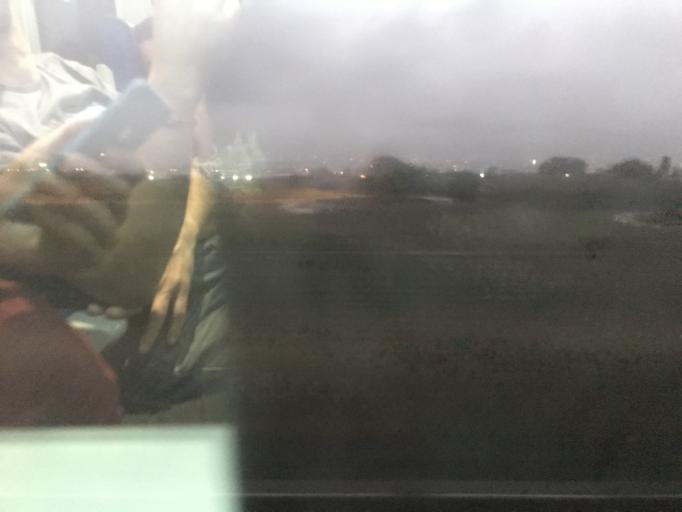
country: TR
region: Kocaeli
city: Derince
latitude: 40.7488
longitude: 29.7971
